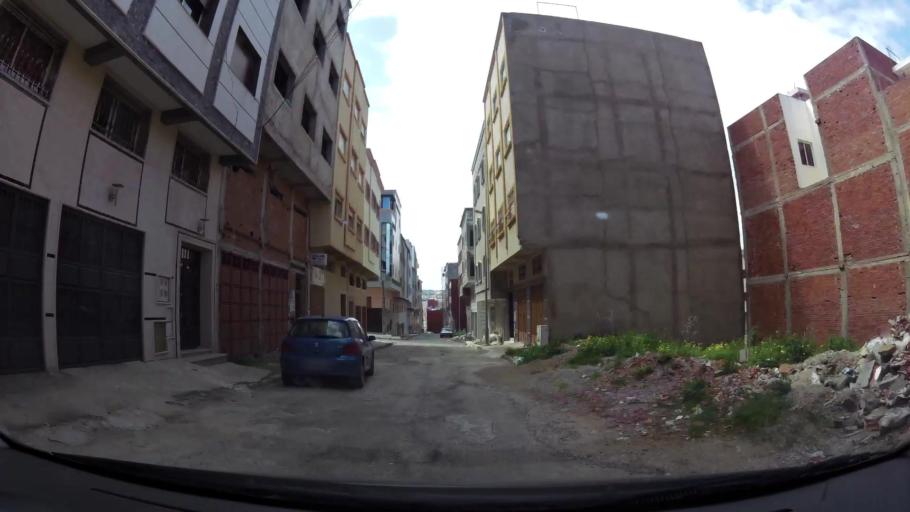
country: MA
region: Tanger-Tetouan
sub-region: Tanger-Assilah
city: Tangier
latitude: 35.7692
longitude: -5.8456
